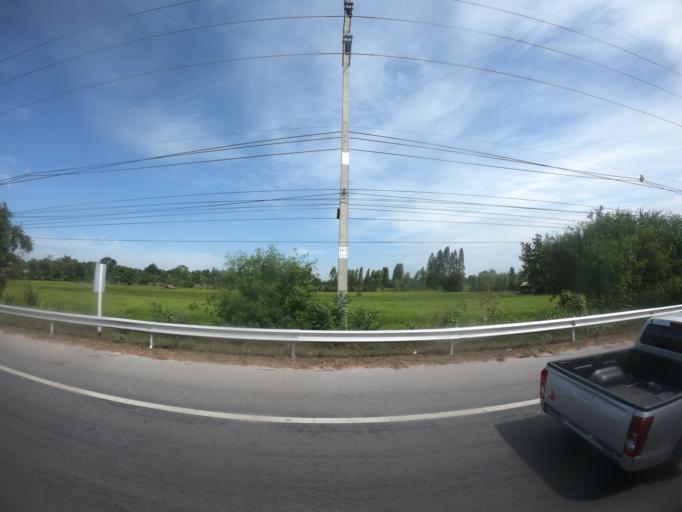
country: TH
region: Maha Sarakham
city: Chiang Yuen
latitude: 16.4461
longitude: 103.0367
